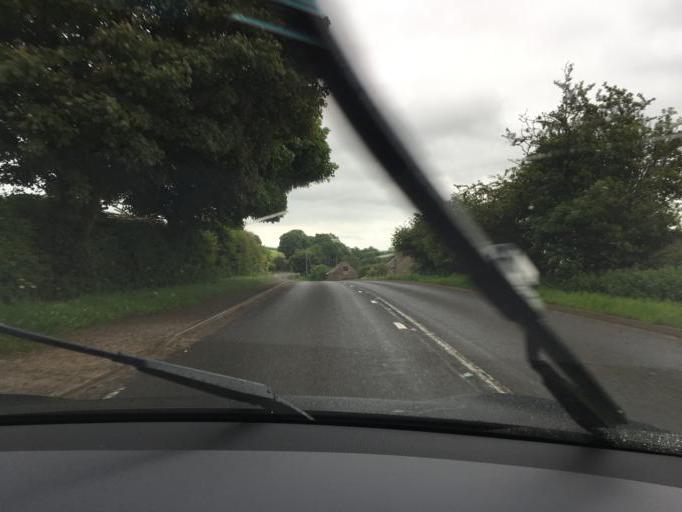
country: GB
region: England
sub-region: Staffordshire
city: Mayfield
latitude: 53.0327
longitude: -1.8061
